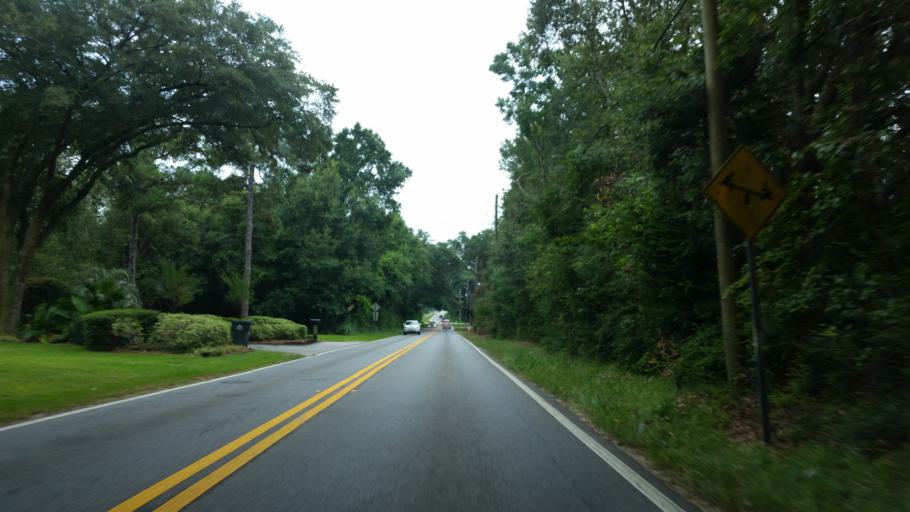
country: US
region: Florida
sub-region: Santa Rosa County
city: Pace
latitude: 30.6352
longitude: -87.1480
